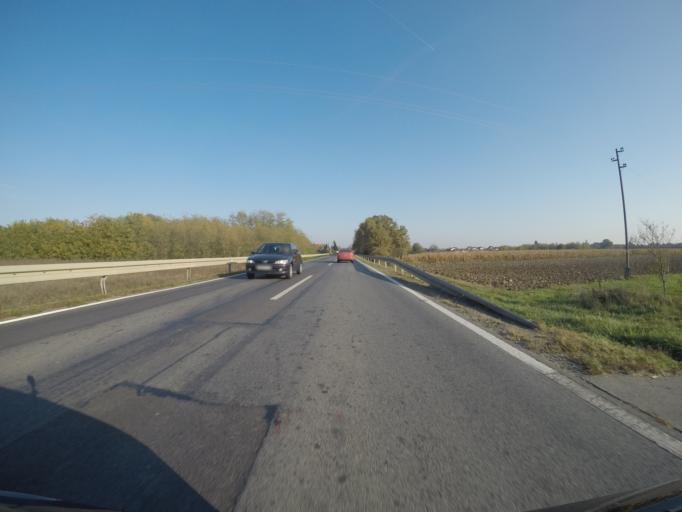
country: HR
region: Virovitick-Podravska
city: Pitomaca
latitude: 45.9651
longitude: 17.2106
